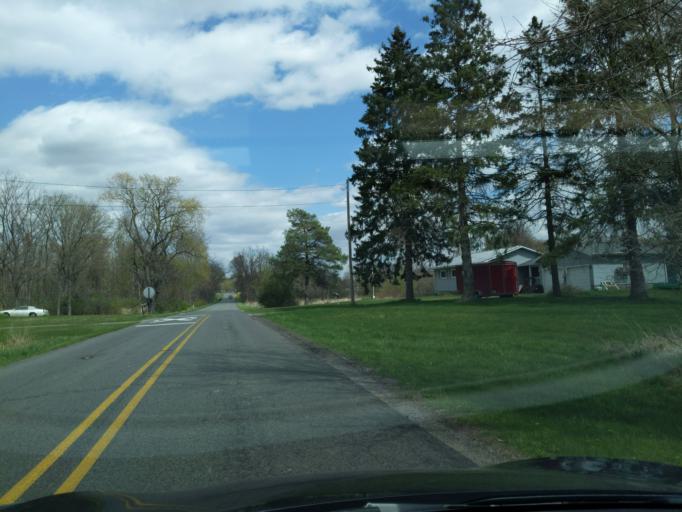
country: US
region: Michigan
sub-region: Ingham County
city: Mason
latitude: 42.6112
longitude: -84.4628
